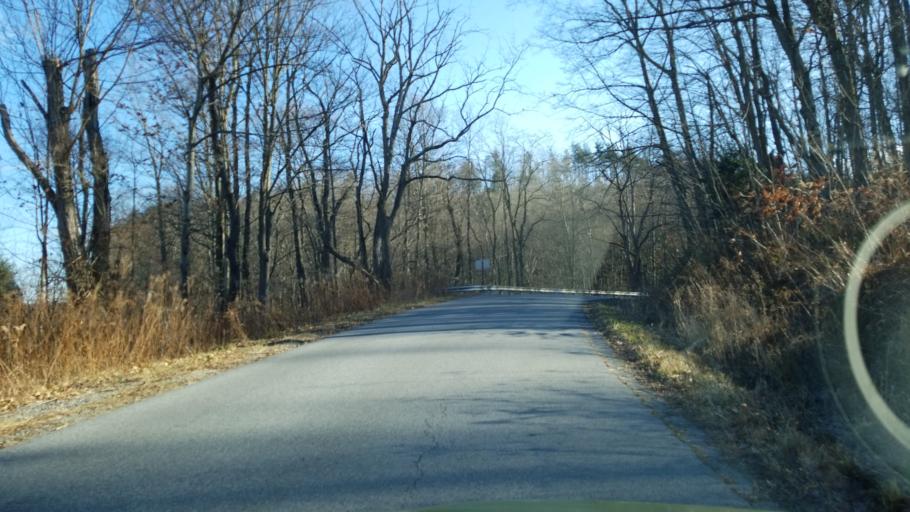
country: US
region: Pennsylvania
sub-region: Clearfield County
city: Hyde
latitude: 40.9852
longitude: -78.4777
